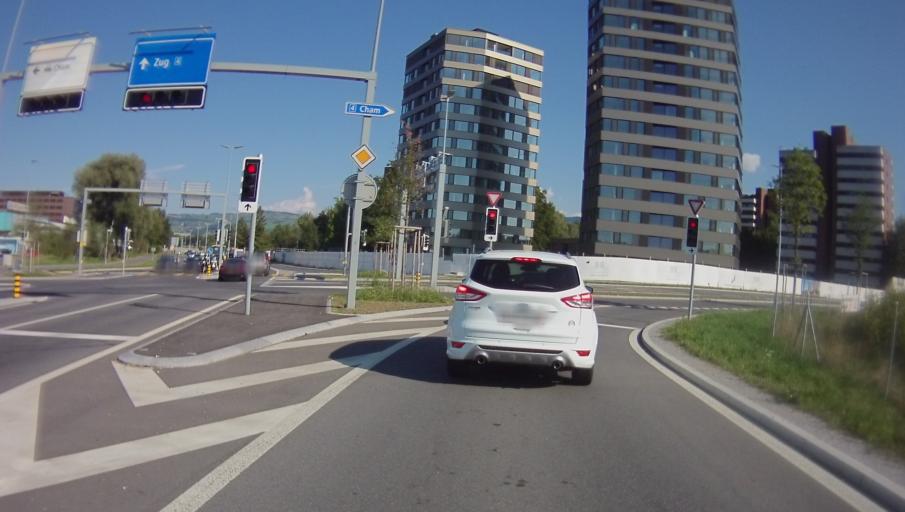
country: CH
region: Zug
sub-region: Zug
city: Cham
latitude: 47.1856
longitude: 8.4737
